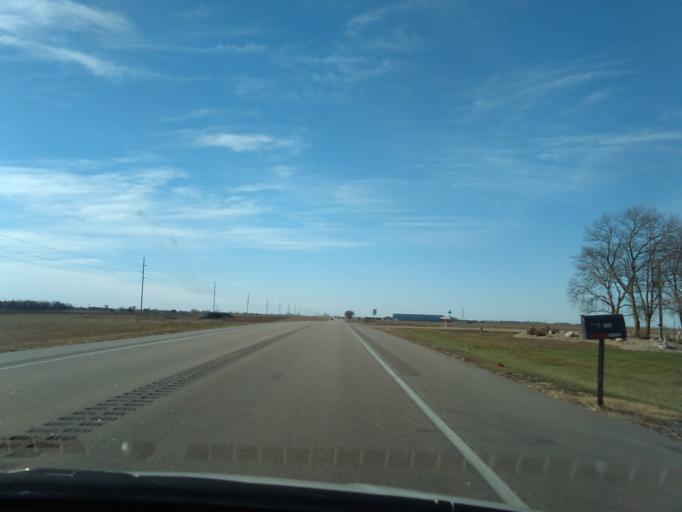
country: US
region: Nebraska
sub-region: Clay County
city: Harvard
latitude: 40.5828
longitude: -98.1644
